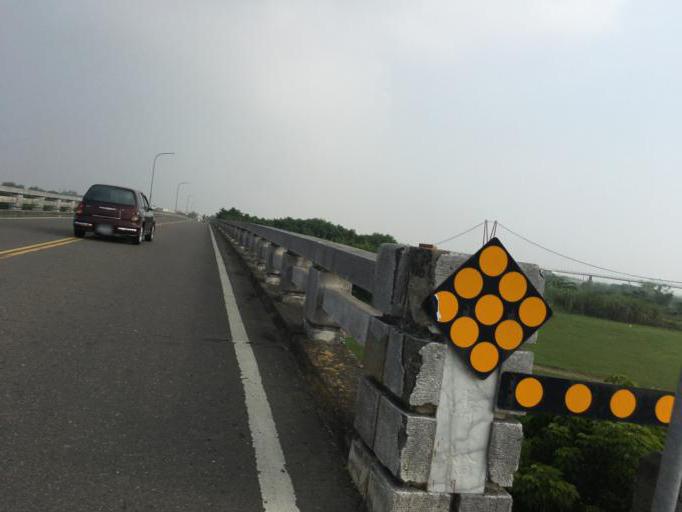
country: TW
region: Taiwan
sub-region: Chiayi
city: Taibao
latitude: 23.4804
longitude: 120.2932
